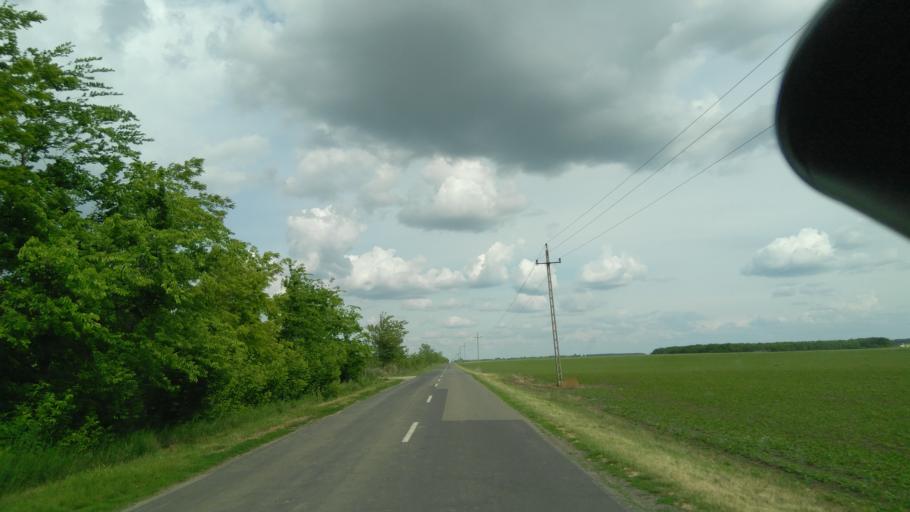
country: HU
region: Bekes
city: Mezohegyes
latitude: 46.3124
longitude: 20.8528
